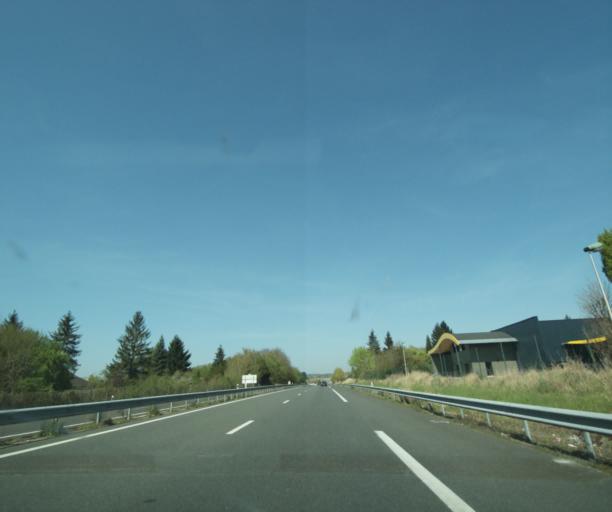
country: FR
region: Bourgogne
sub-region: Departement de la Nievre
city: Pouilly-sur-Loire
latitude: 47.2656
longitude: 2.9822
